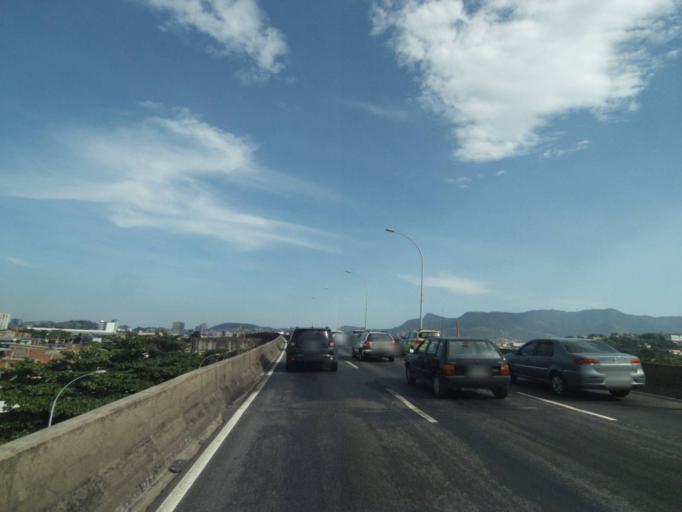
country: BR
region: Rio de Janeiro
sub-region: Rio De Janeiro
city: Rio de Janeiro
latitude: -22.8828
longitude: -43.2306
